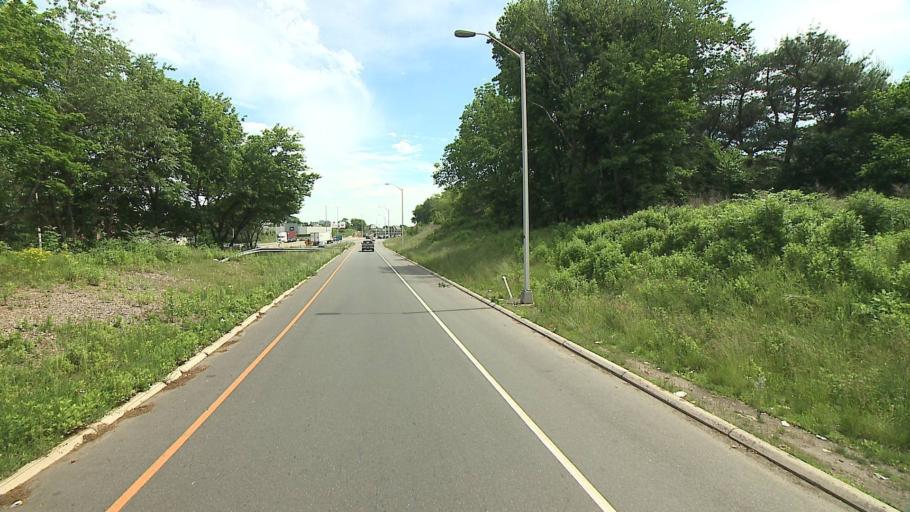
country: US
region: Connecticut
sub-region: Fairfield County
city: Norwalk
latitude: 41.1009
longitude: -73.4357
